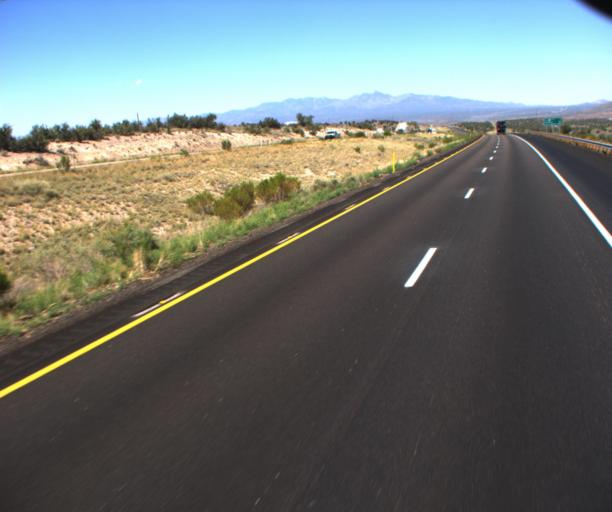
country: US
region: Arizona
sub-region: Mohave County
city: Peach Springs
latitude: 35.1624
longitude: -113.5819
